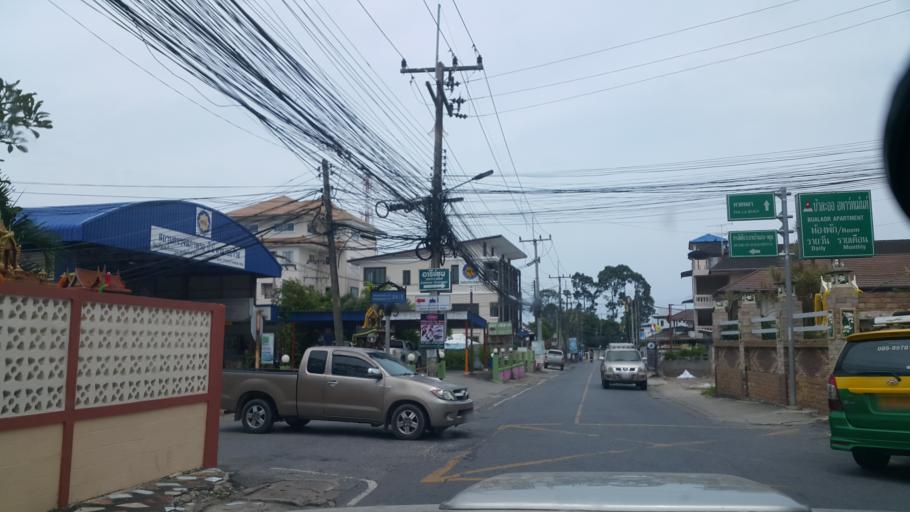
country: TH
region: Rayong
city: Ban Chang
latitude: 12.7194
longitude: 101.0484
